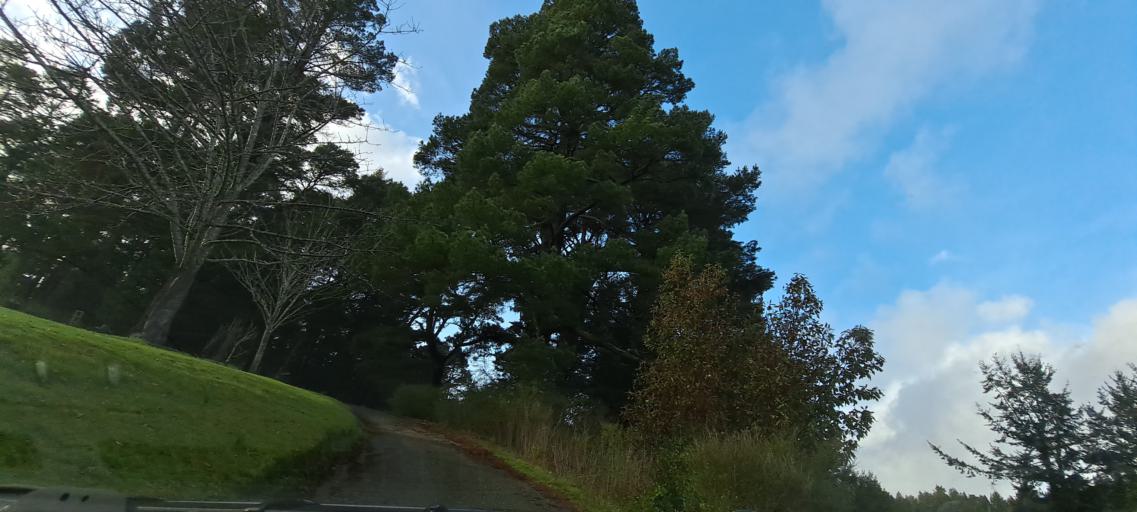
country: US
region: California
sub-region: Humboldt County
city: Fortuna
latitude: 40.6034
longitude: -124.1591
